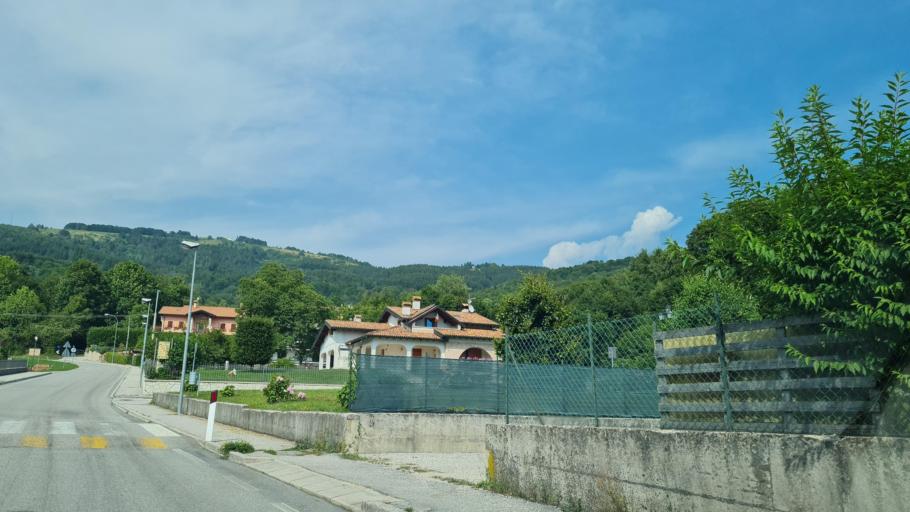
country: IT
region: Veneto
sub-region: Provincia di Vicenza
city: Conco
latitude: 45.7978
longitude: 11.6319
